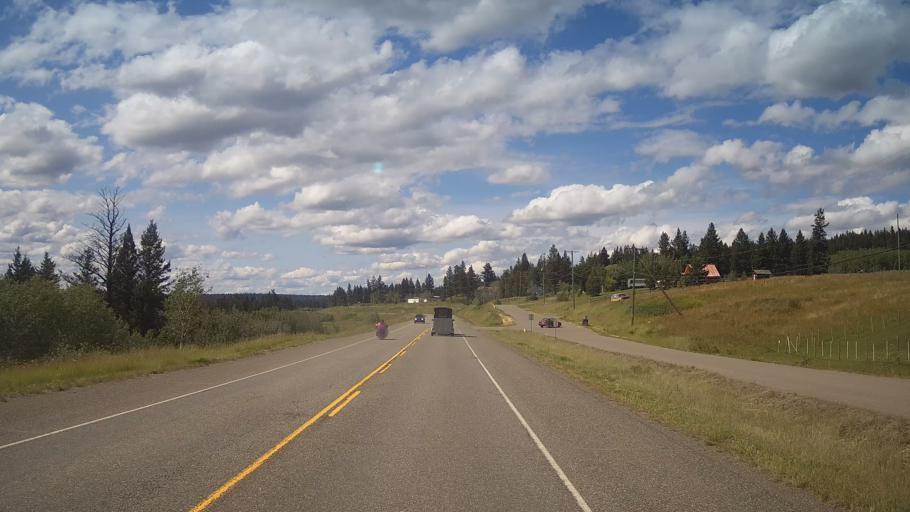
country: CA
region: British Columbia
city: Williams Lake
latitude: 51.8345
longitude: -121.5496
